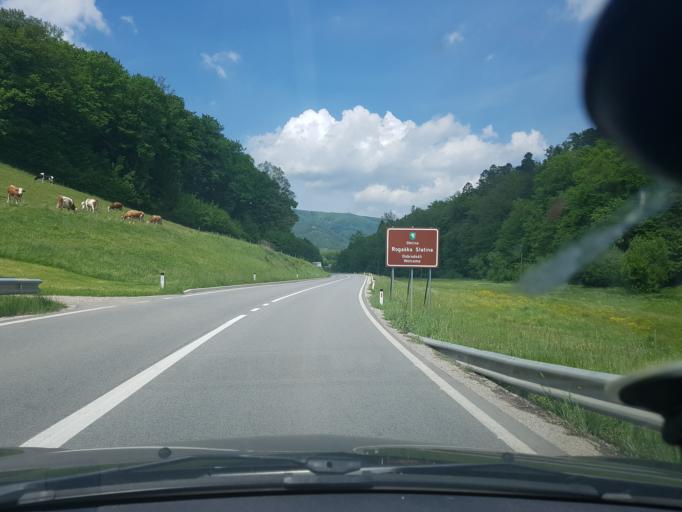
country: SI
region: Rogatec
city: Rogatec
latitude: 46.2289
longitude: 15.6752
